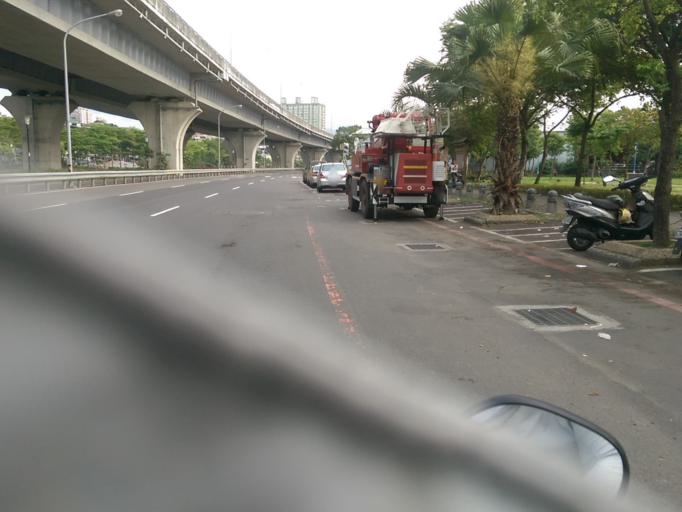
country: TW
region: Taipei
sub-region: Taipei
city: Banqiao
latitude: 25.0146
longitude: 121.4497
